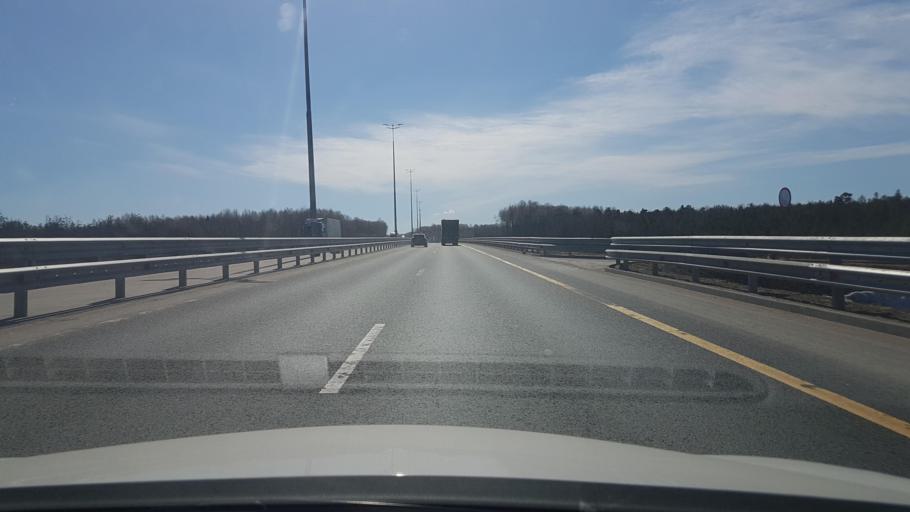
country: RU
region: Novgorod
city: Krechevitsy
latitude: 58.9662
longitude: 31.3496
